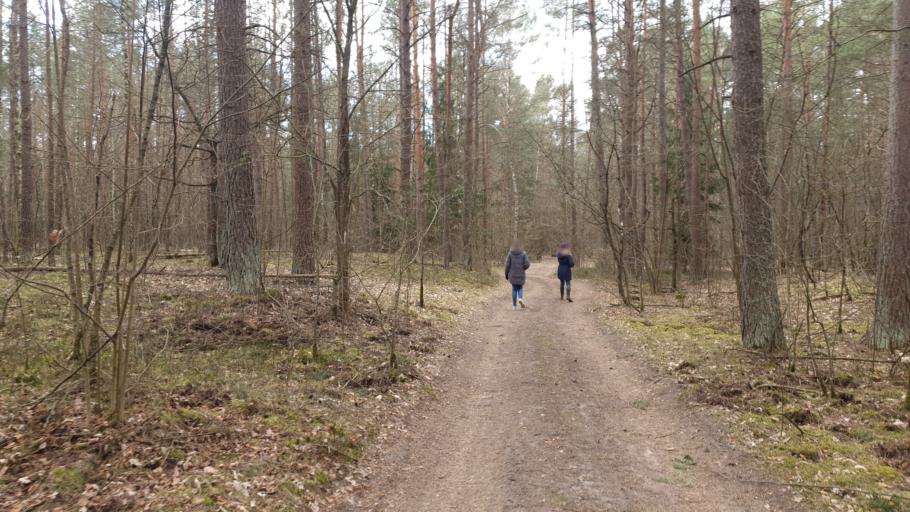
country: LT
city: Grigiskes
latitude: 54.7280
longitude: 25.0335
